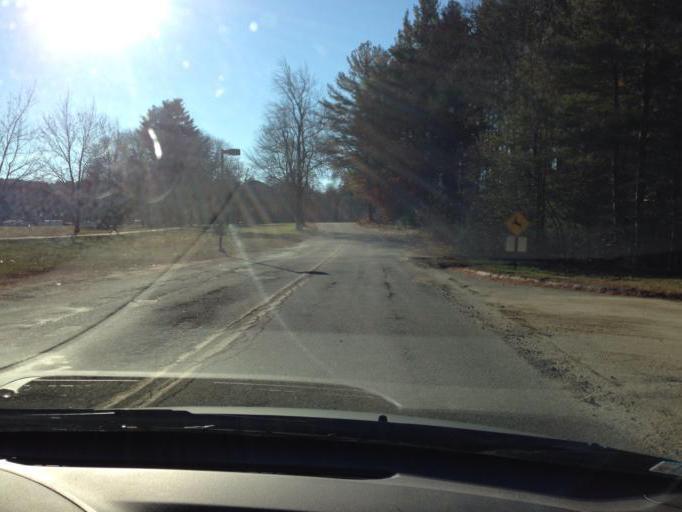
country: US
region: Massachusetts
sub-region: Middlesex County
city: Bedford
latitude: 42.5027
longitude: -71.2725
